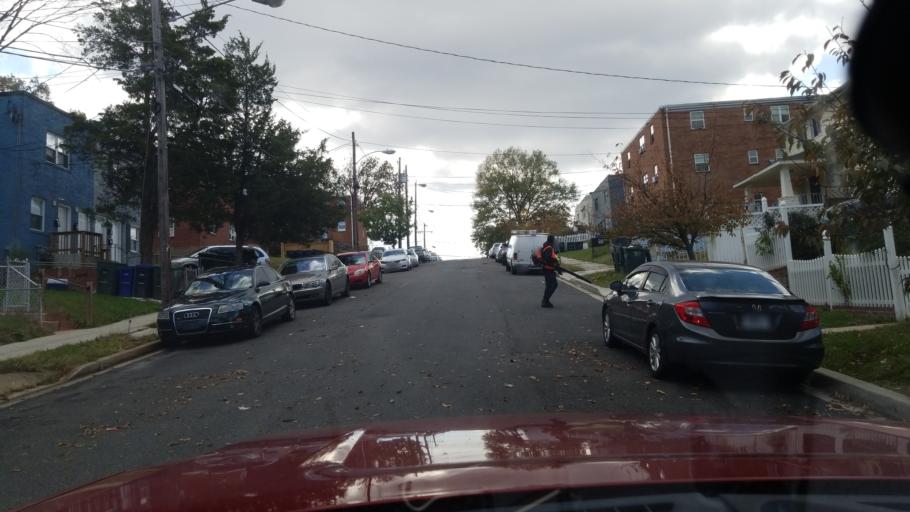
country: US
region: Maryland
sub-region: Prince George's County
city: Fairmount Heights
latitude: 38.8971
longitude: -76.9165
